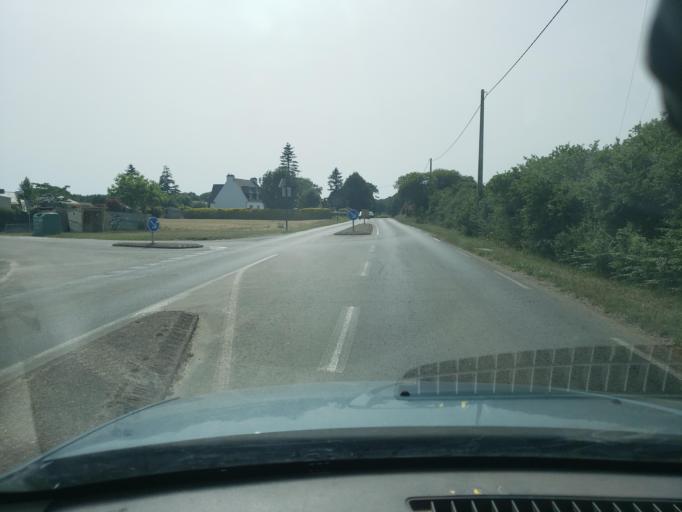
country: FR
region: Brittany
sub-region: Departement du Finistere
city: Plobannalec-Lesconil
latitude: 47.8225
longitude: -4.2378
